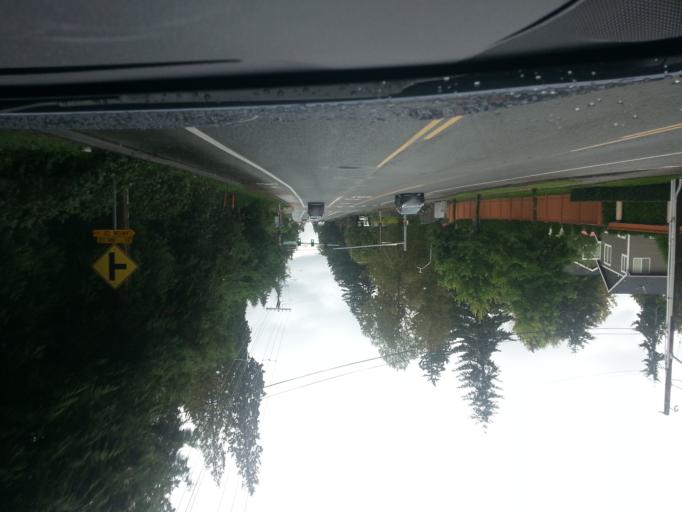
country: US
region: Washington
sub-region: King County
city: Bothell
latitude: 47.7912
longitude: -122.1933
